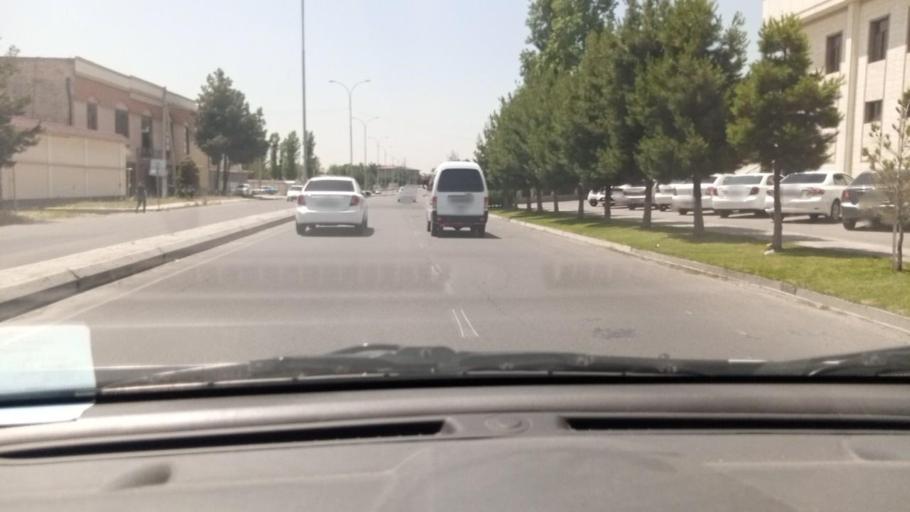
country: UZ
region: Toshkent Shahri
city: Tashkent
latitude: 41.2494
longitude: 69.2107
